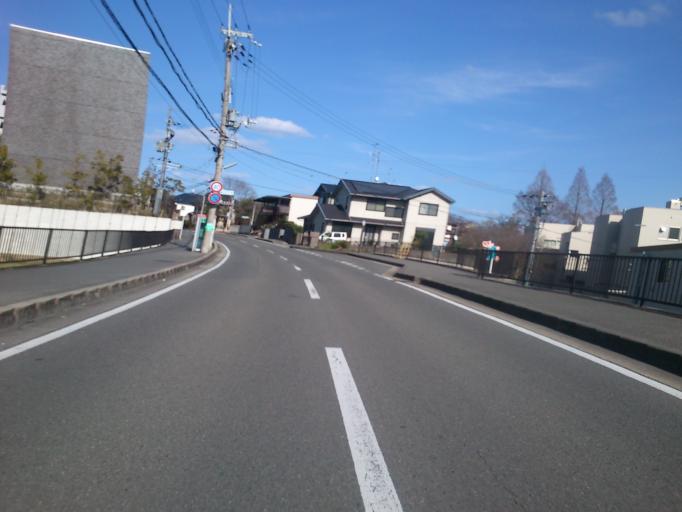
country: JP
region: Kyoto
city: Muko
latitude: 34.9217
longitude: 135.6809
